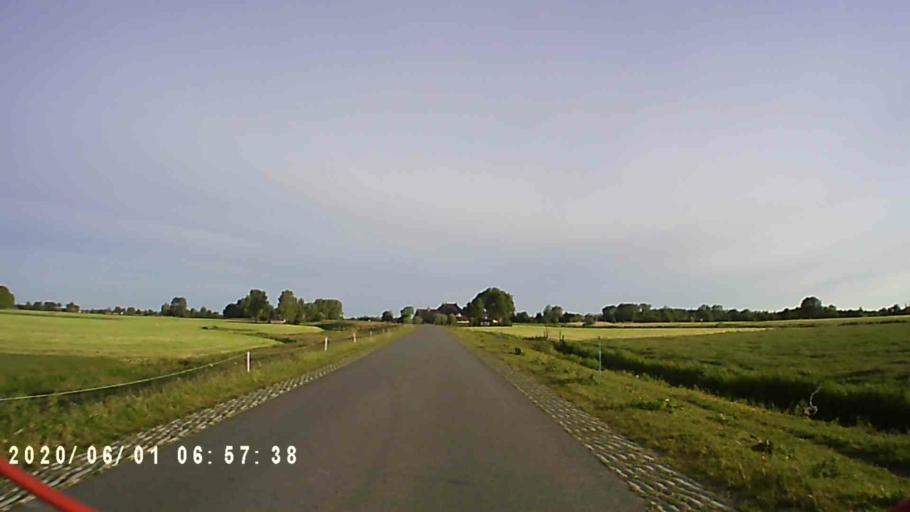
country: NL
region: Friesland
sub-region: Gemeente Dongeradeel
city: Anjum
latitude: 53.3184
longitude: 6.1060
